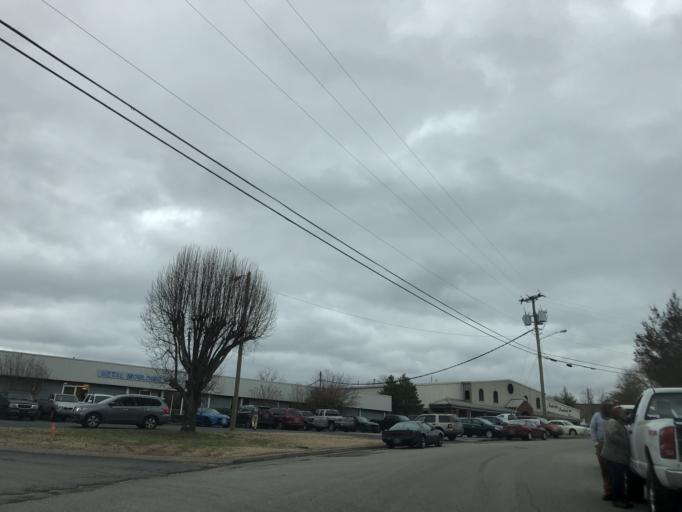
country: US
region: Tennessee
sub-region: Davidson County
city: Goodlettsville
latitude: 36.2855
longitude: -86.6893
